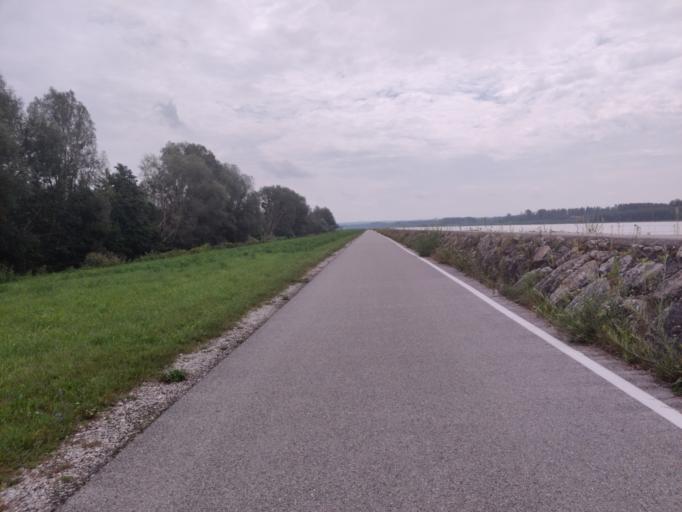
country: AT
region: Upper Austria
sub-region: Politischer Bezirk Perg
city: Perg
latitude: 48.2170
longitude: 14.5942
